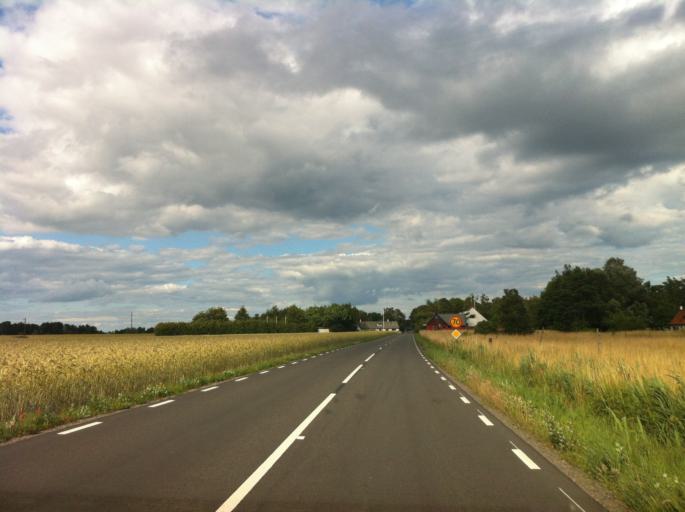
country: SE
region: Skane
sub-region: Simrishamns Kommun
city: Simrishamn
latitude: 55.3948
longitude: 14.1768
